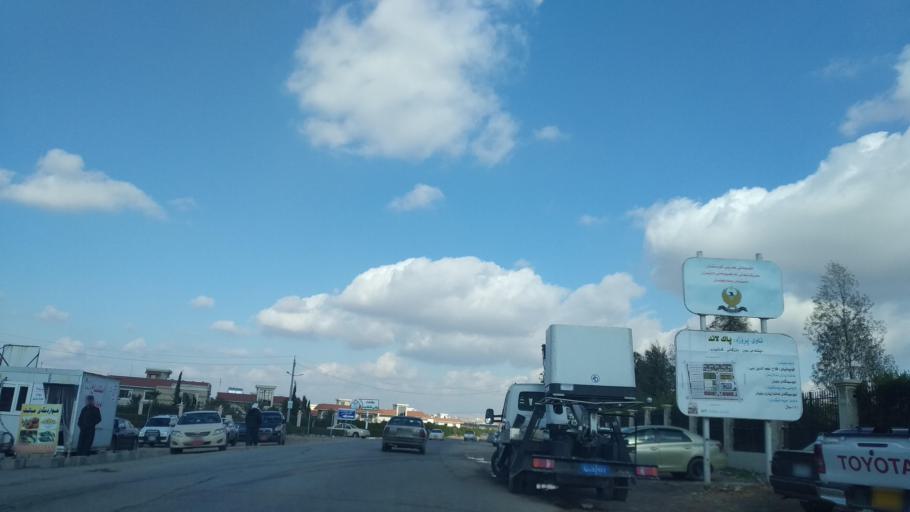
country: IQ
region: Arbil
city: Erbil
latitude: 36.2083
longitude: 44.1339
